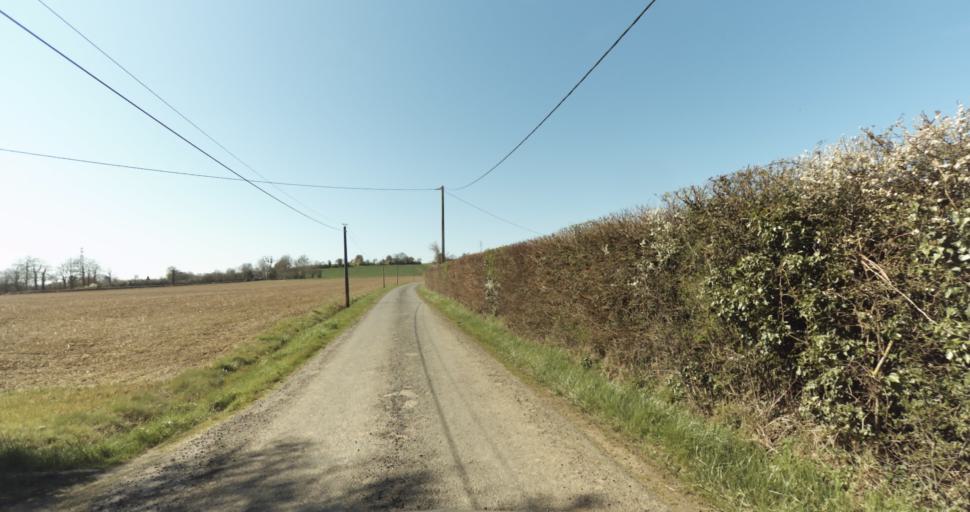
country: FR
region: Lower Normandy
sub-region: Departement du Calvados
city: Saint-Pierre-sur-Dives
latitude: 49.0543
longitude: -0.0052
